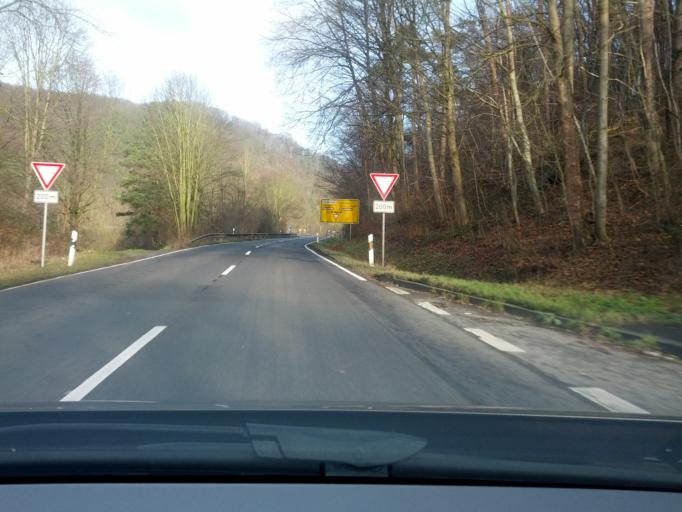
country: DE
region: Thuringia
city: Lindewerra
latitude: 51.3216
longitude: 9.9049
